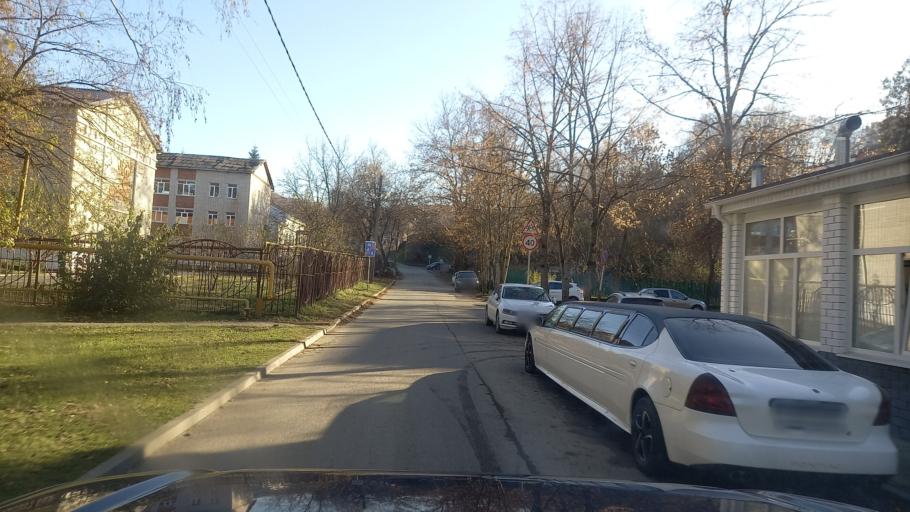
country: RU
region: Krasnodarskiy
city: Goryachiy Klyuch
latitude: 44.6265
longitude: 39.1054
